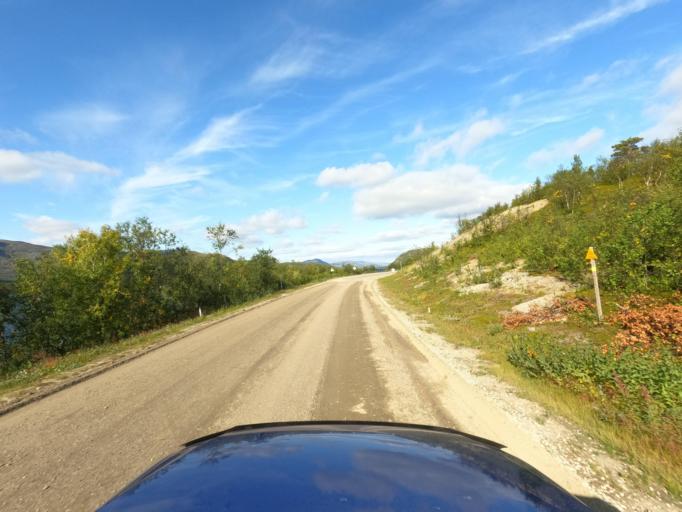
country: NO
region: Finnmark Fylke
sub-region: Porsanger
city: Lakselv
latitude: 69.8942
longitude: 24.9919
